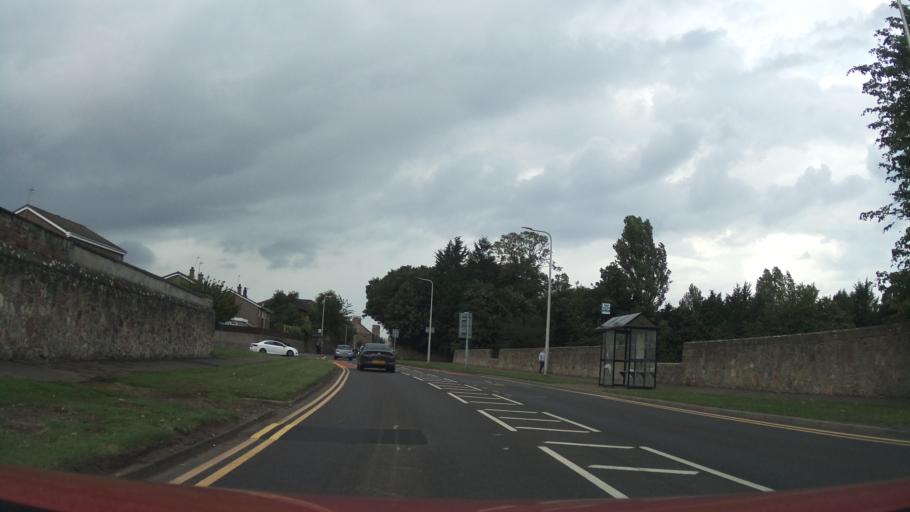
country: GB
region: Scotland
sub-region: East Lothian
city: Musselburgh
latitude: 55.9412
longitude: -3.0397
